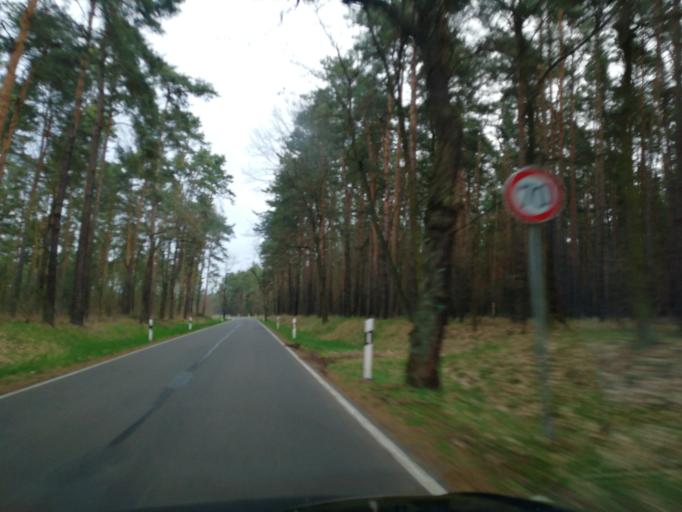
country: DE
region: Brandenburg
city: Vetschau
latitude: 51.7345
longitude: 14.1276
